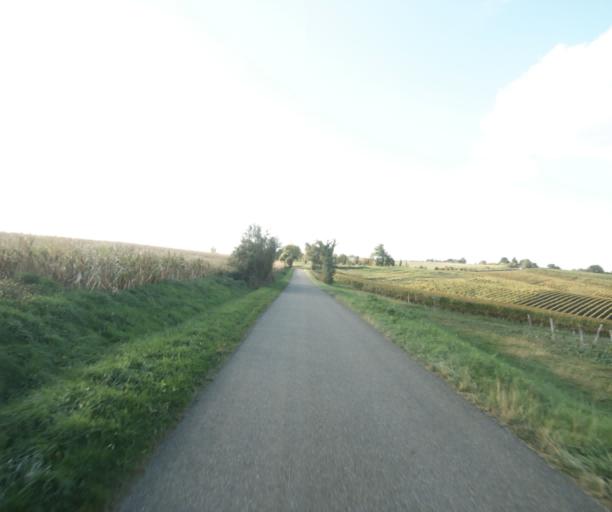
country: FR
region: Midi-Pyrenees
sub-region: Departement du Gers
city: Eauze
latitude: 43.7418
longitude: 0.1388
